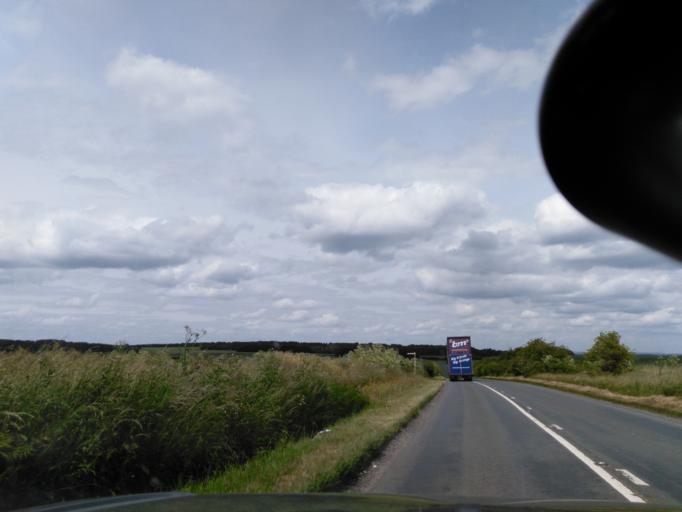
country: GB
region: England
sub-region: Wiltshire
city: Woodford
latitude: 51.1342
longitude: -1.8573
